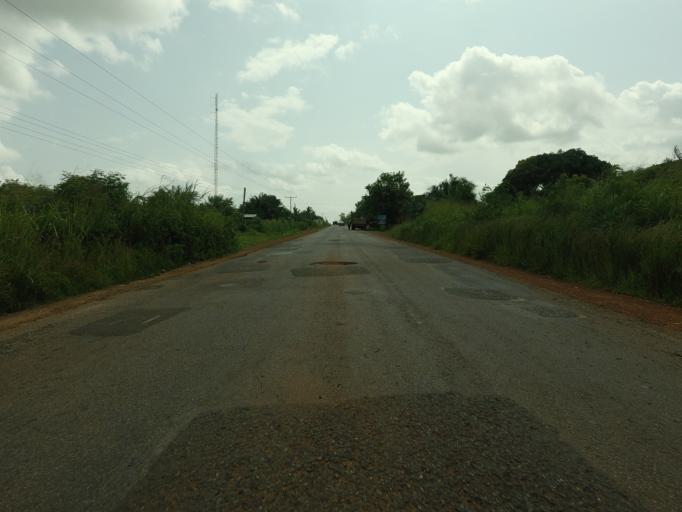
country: TG
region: Maritime
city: Lome
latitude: 6.2251
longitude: 1.0258
